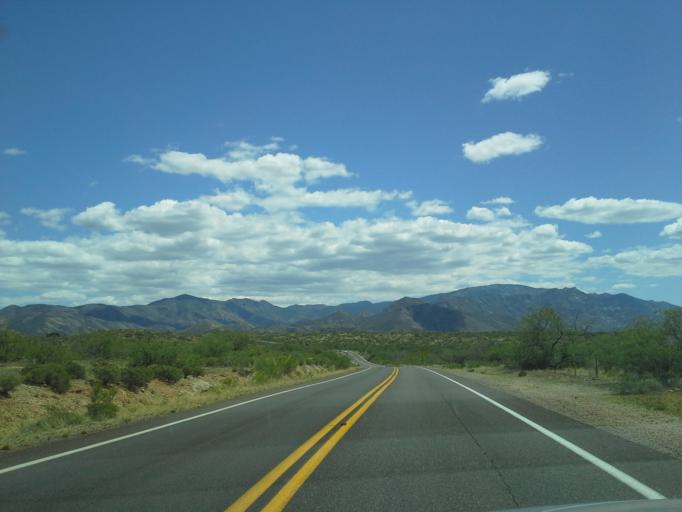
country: US
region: Arizona
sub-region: Pinal County
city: Oracle
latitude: 32.5976
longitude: -110.8539
